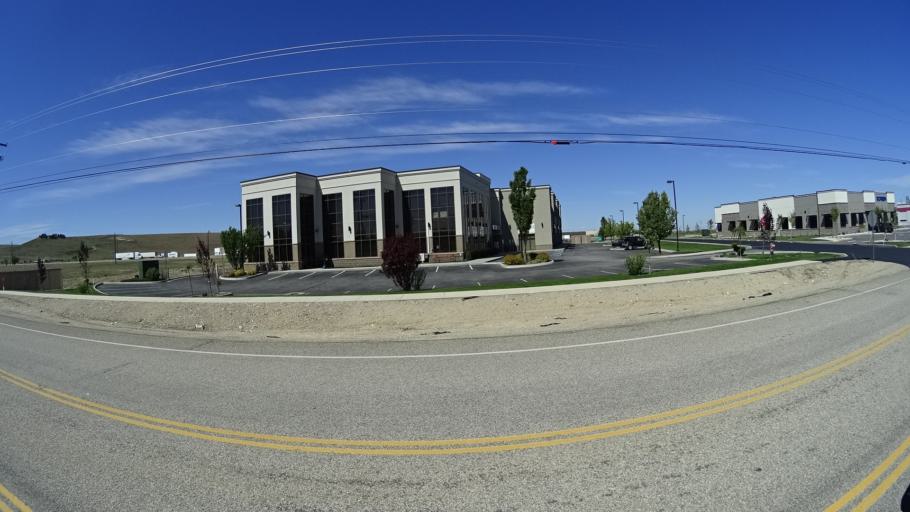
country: US
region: Idaho
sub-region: Ada County
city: Boise
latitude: 43.5195
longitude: -116.1461
